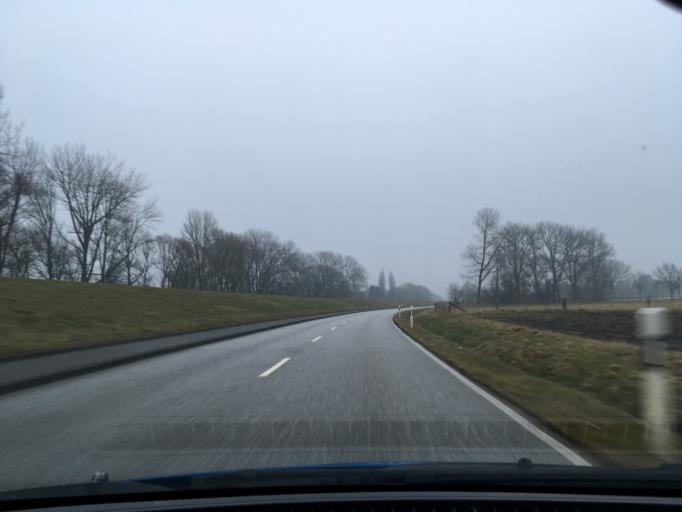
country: DE
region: Hamburg
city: Harburg
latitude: 53.4717
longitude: 10.0305
